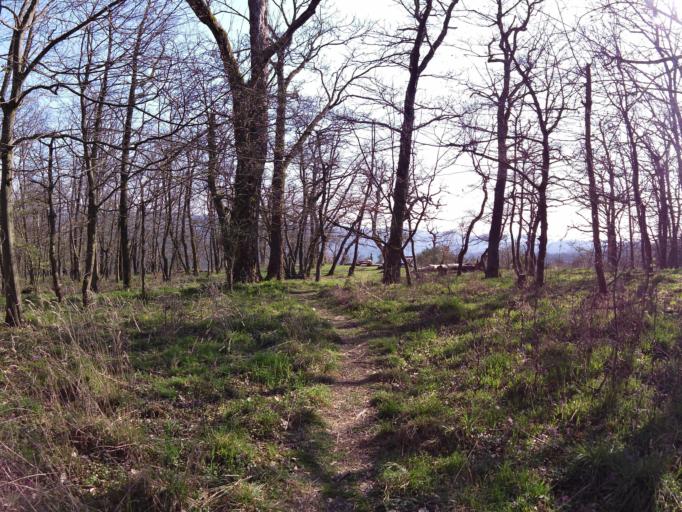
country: DE
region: Thuringia
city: Eisenach
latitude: 50.9621
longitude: 10.3083
